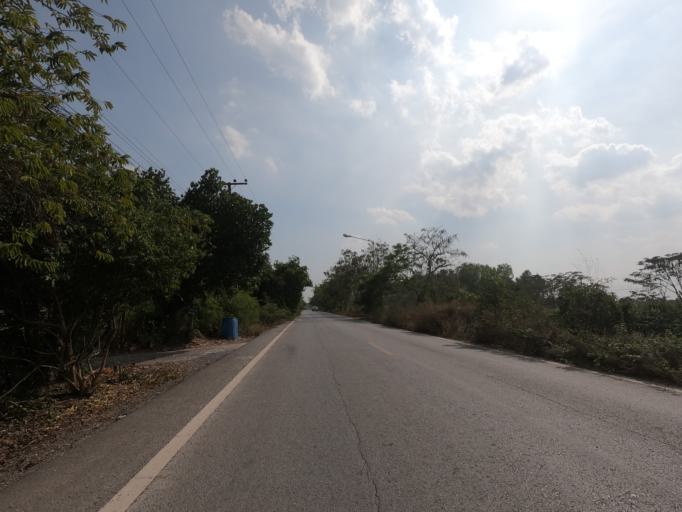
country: TH
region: Pathum Thani
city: Nong Suea
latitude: 14.1174
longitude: 100.8465
